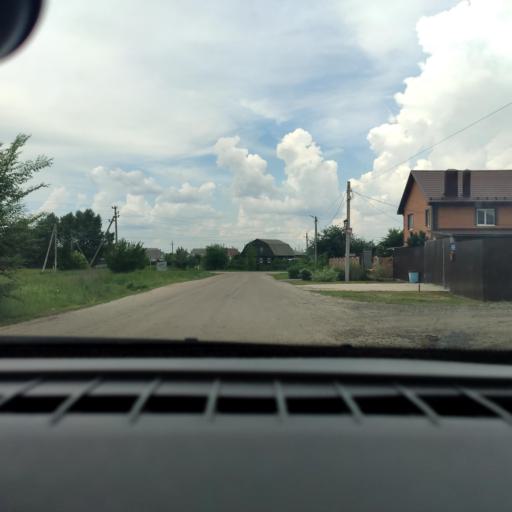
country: RU
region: Voronezj
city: Novaya Usman'
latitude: 51.5996
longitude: 39.3250
